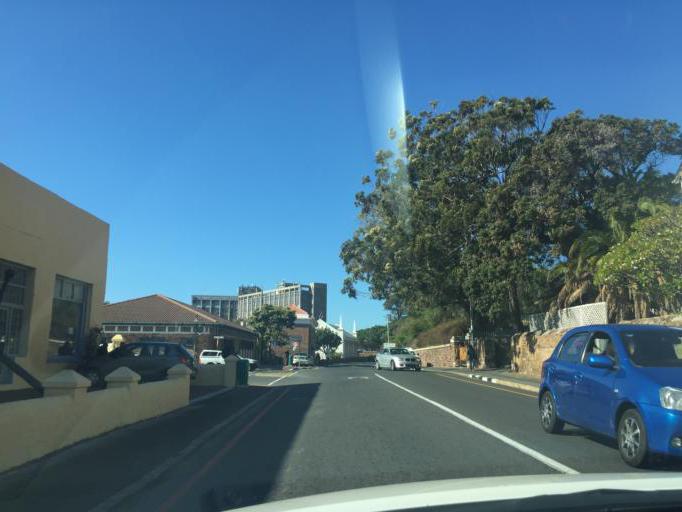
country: ZA
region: Western Cape
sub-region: City of Cape Town
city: Retreat
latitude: -34.1934
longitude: 18.4355
